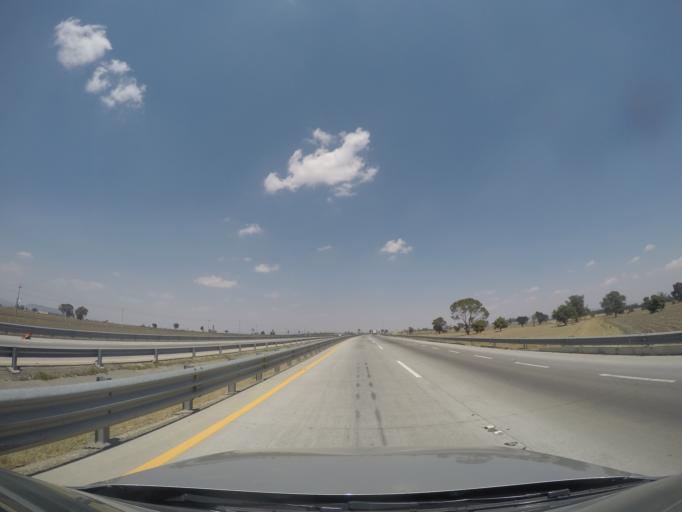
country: MX
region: Tlaxcala
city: Sanctorum
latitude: 19.5300
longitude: -98.4808
